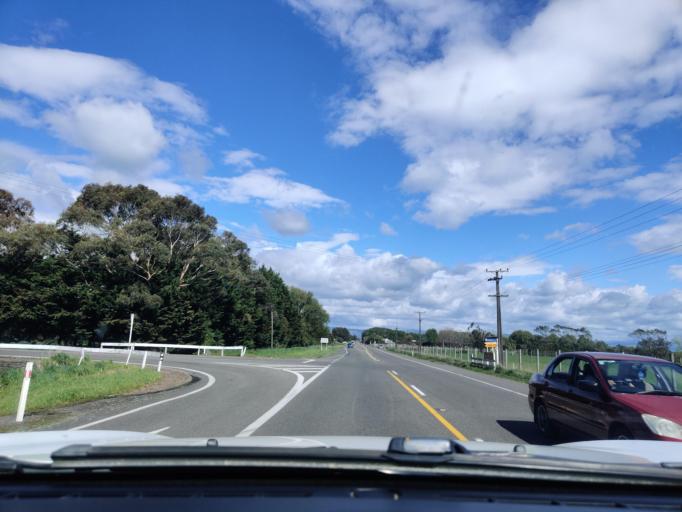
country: NZ
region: Manawatu-Wanganui
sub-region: Palmerston North City
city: Palmerston North
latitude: -40.2902
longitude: 175.5356
